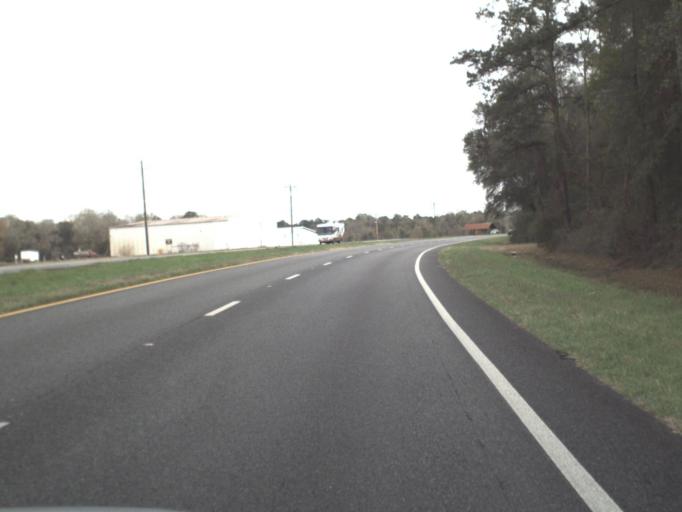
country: US
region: Florida
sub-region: Gadsden County
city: Havana
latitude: 30.5490
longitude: -84.3780
